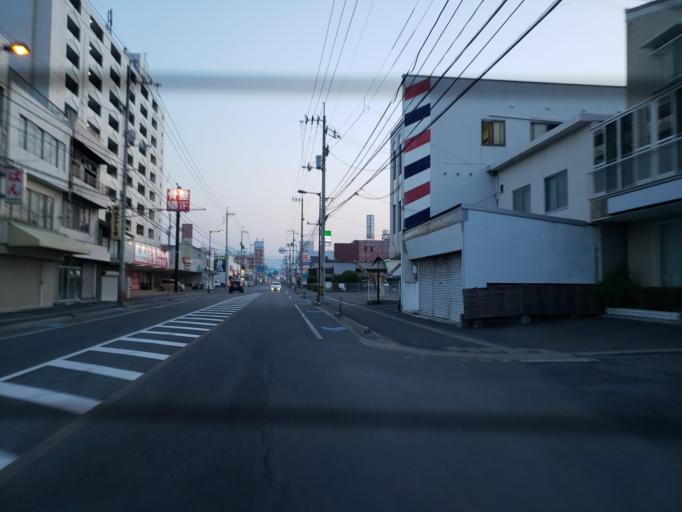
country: JP
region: Ehime
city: Hojo
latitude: 34.0543
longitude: 132.9868
